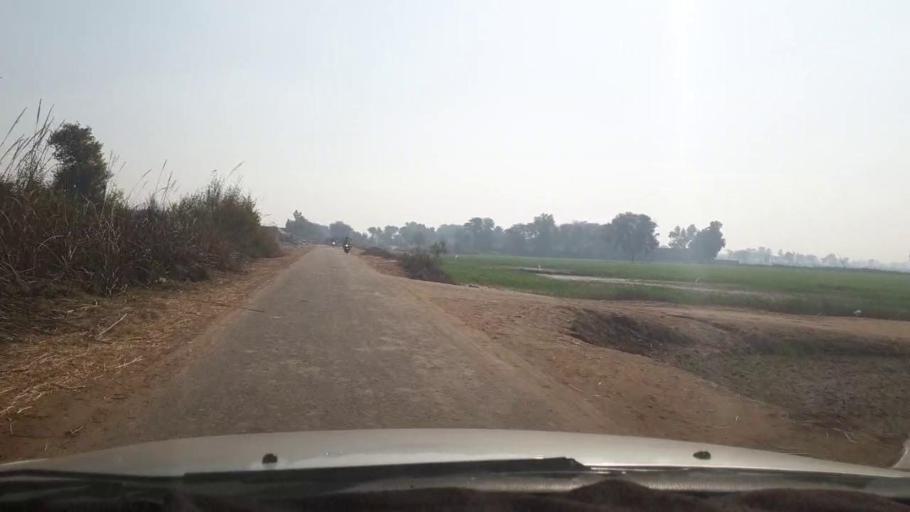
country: PK
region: Sindh
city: Khanpur
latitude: 27.7310
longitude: 69.5141
